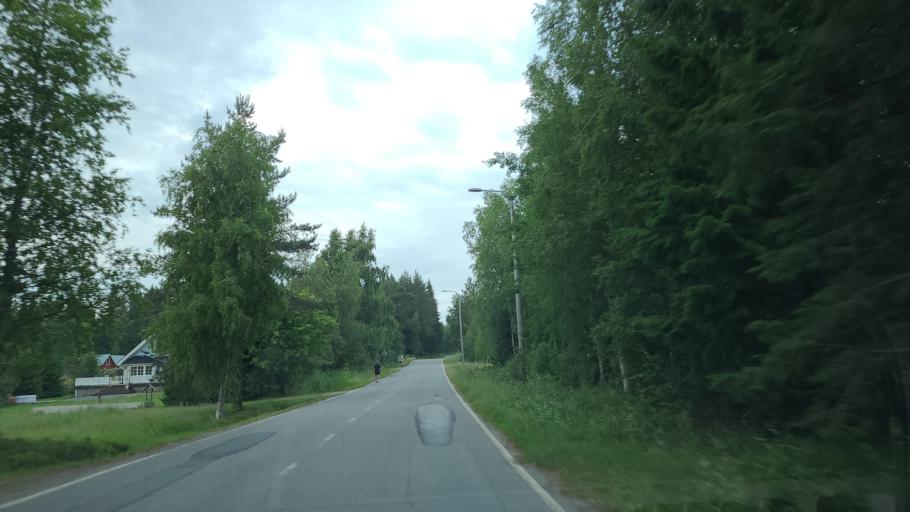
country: FI
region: Ostrobothnia
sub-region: Vaasa
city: Replot
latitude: 63.1720
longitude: 21.2766
